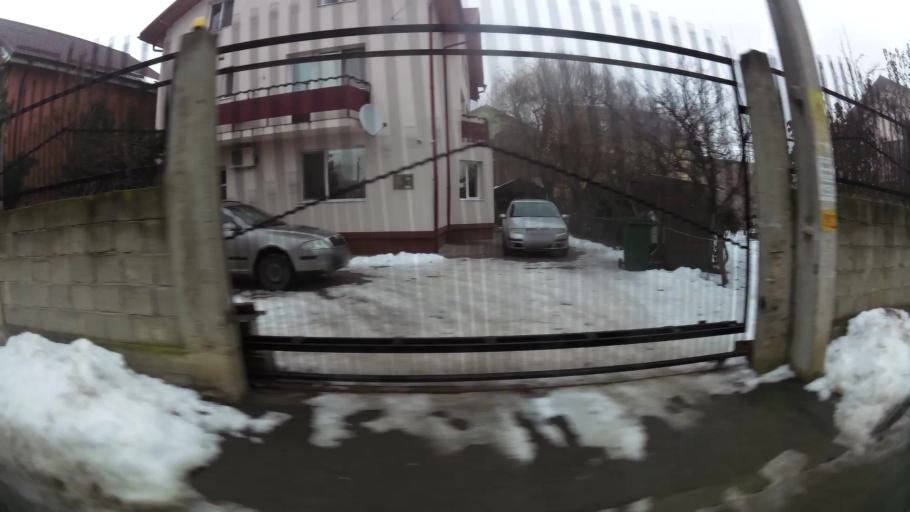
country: RO
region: Ilfov
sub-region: Comuna Chiajna
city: Rosu
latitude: 44.4565
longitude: 25.9968
